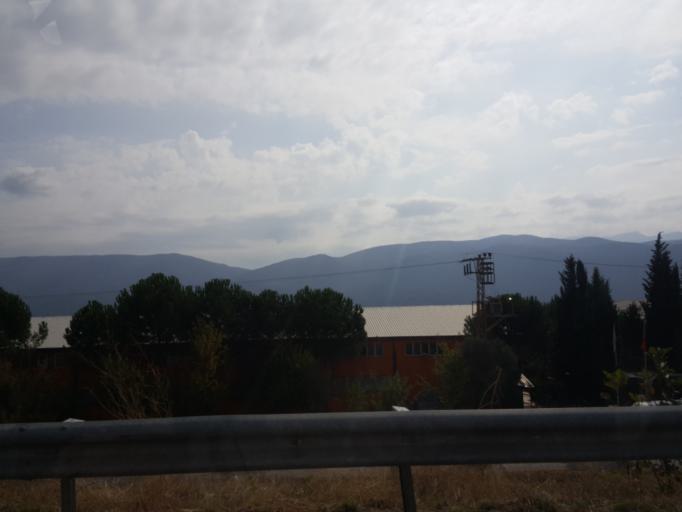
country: TR
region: Corum
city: Kargi
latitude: 41.1353
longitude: 34.4642
